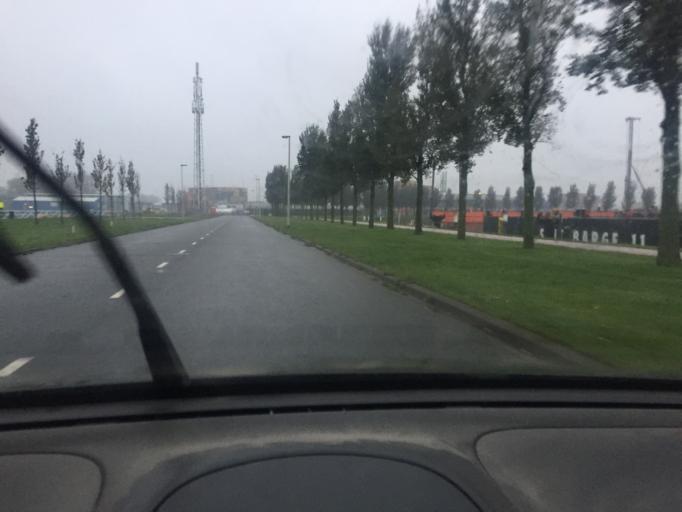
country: NL
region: South Holland
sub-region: Gemeente Schiedam
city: Schiedam
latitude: 51.8941
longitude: 4.4123
